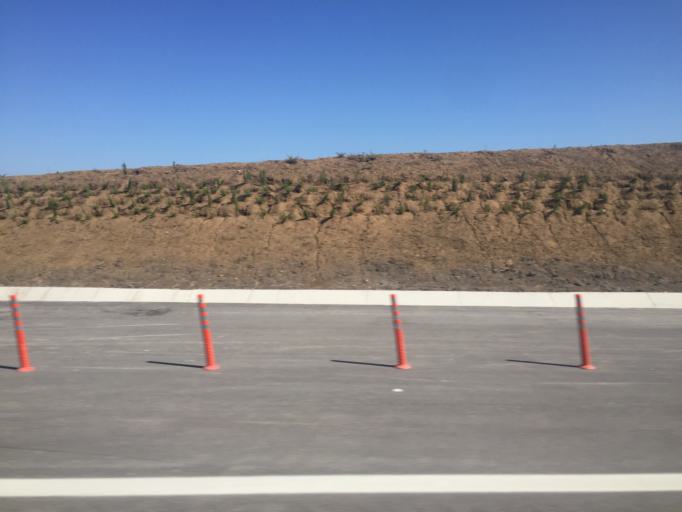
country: TR
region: Bursa
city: Mahmudiye
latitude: 40.2650
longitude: 28.6588
